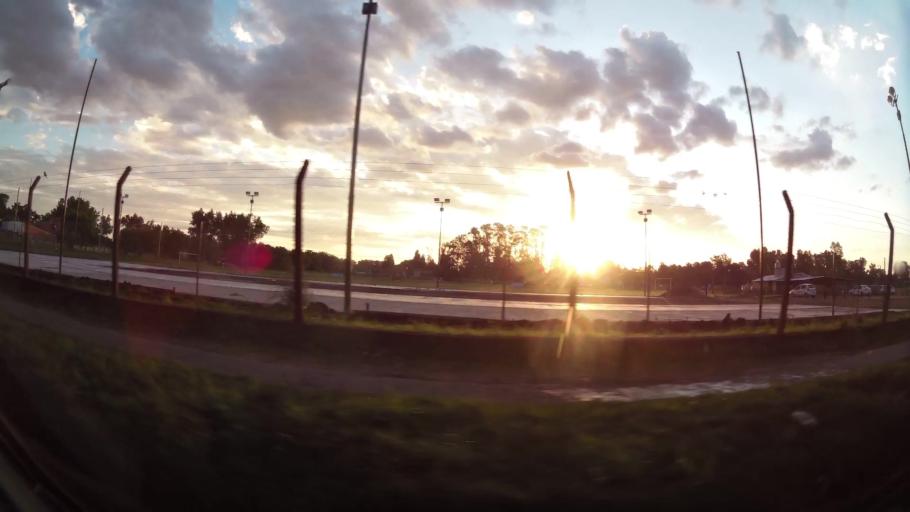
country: AR
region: Buenos Aires
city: Santa Catalina - Dique Lujan
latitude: -34.4806
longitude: -58.7534
